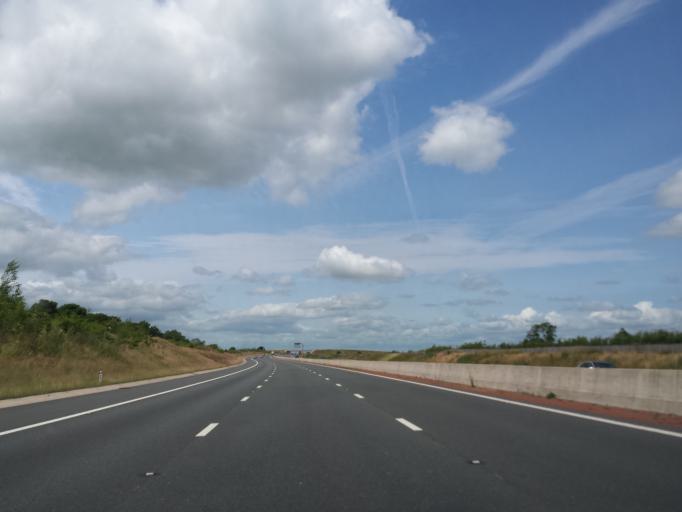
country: GB
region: England
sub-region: North Yorkshire
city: Ripon
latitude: 54.2304
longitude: -1.4921
